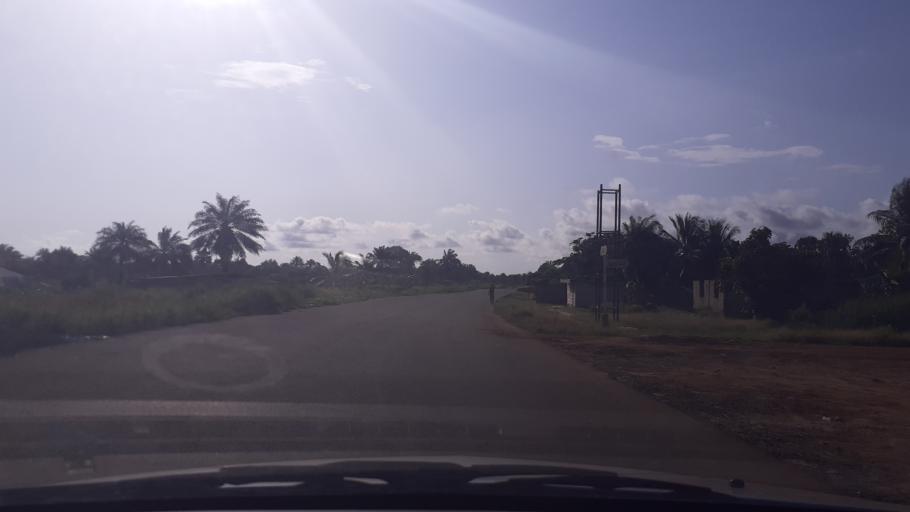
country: LR
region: Montserrado
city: Bensonville City
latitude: 6.1685
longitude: -10.4450
